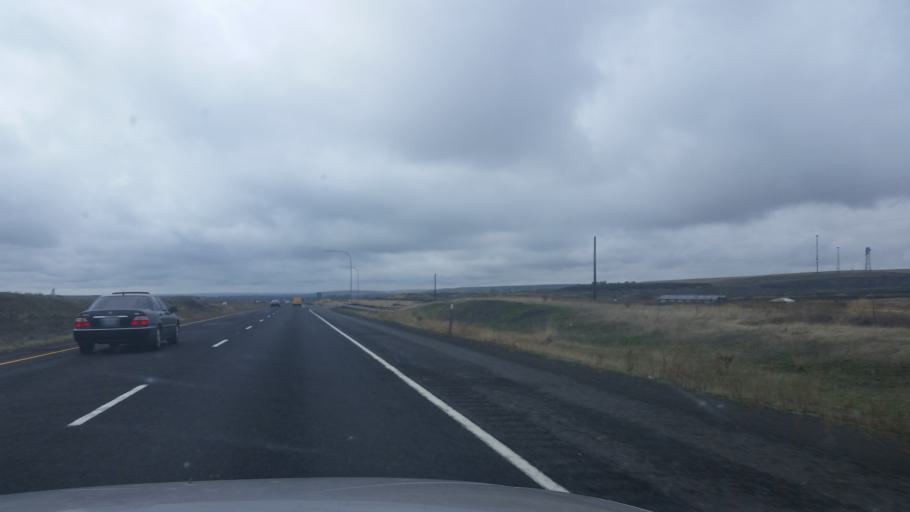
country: US
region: Washington
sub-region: Spokane County
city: Medical Lake
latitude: 47.3109
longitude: -117.9673
